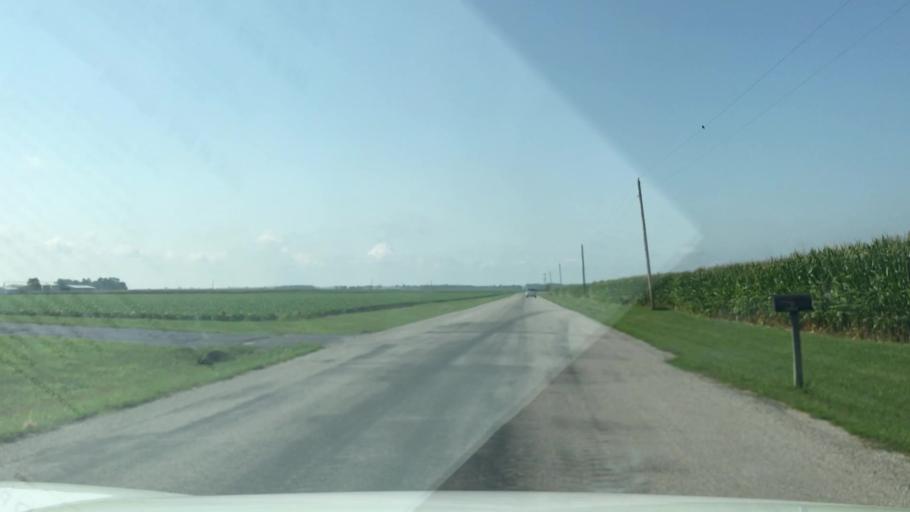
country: US
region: Illinois
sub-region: Washington County
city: Okawville
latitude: 38.4174
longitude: -89.4777
